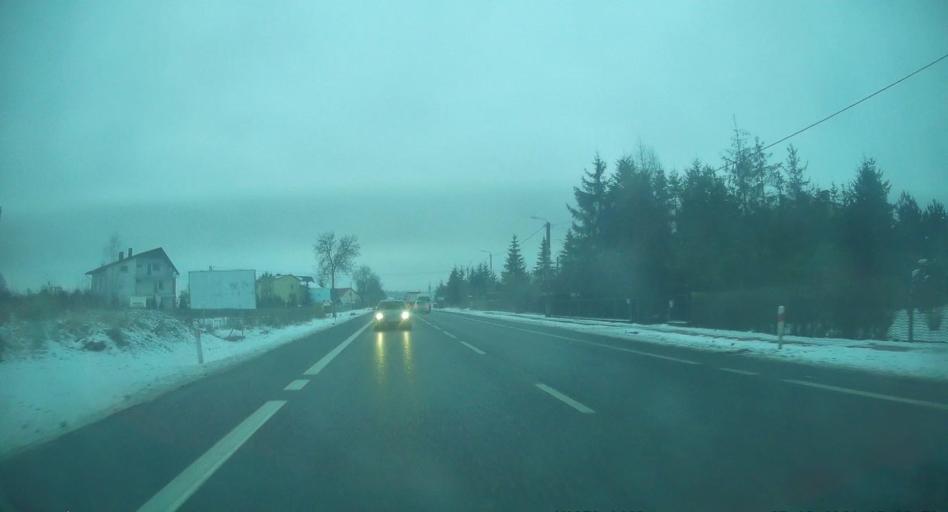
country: PL
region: Swietokrzyskie
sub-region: Powiat kielecki
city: Kostomloty Drugie
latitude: 50.9172
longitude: 20.5718
